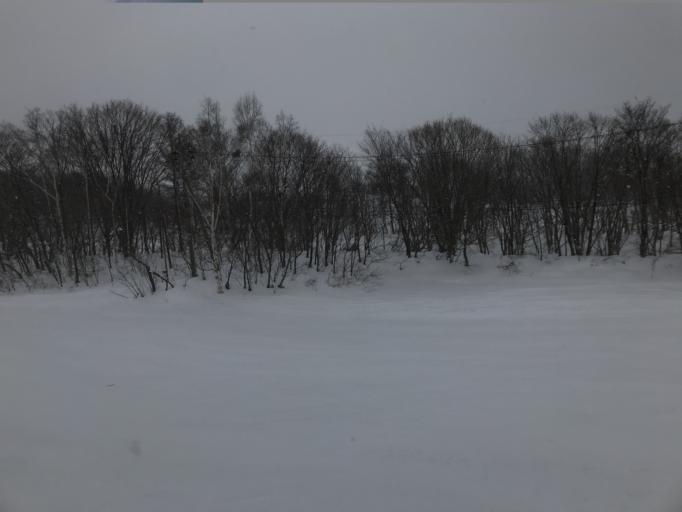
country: JP
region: Nagano
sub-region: Kitaazumi Gun
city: Hakuba
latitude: 36.7554
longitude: 137.8615
